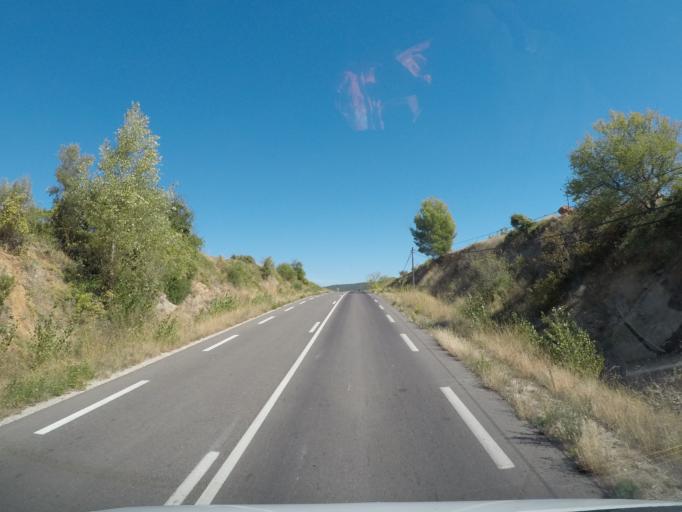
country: FR
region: Languedoc-Roussillon
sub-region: Departement de l'Herault
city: Aniane
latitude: 43.7062
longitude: 3.6003
